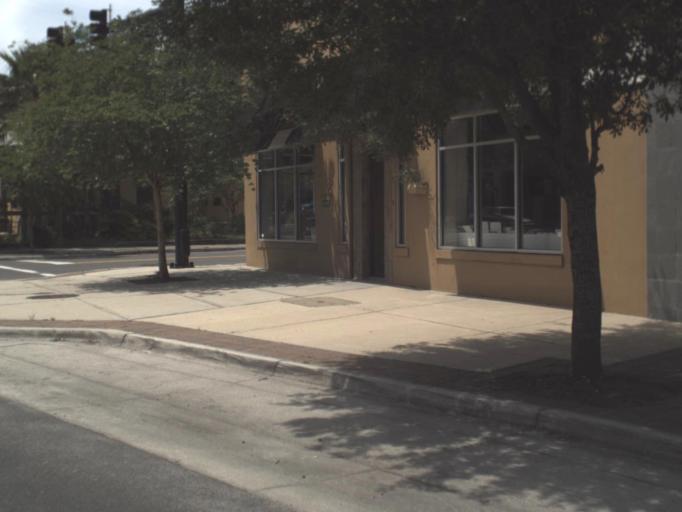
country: US
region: Florida
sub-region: Duval County
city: Jacksonville
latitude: 30.3076
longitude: -81.6544
